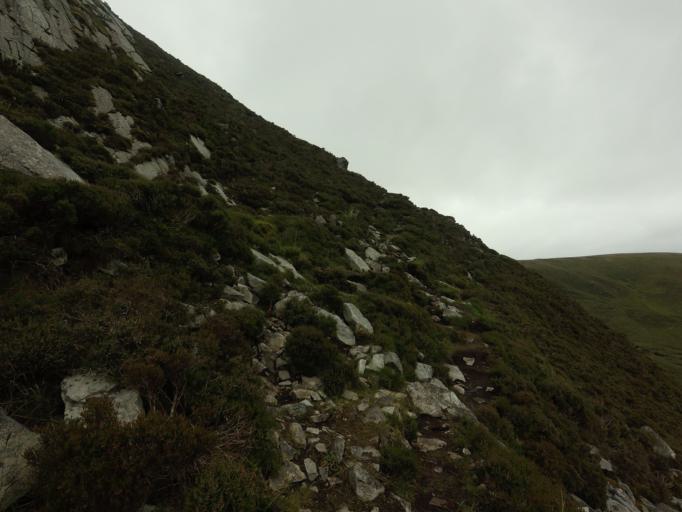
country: IE
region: Ulster
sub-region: County Donegal
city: Killybegs
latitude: 54.6446
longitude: -8.6874
